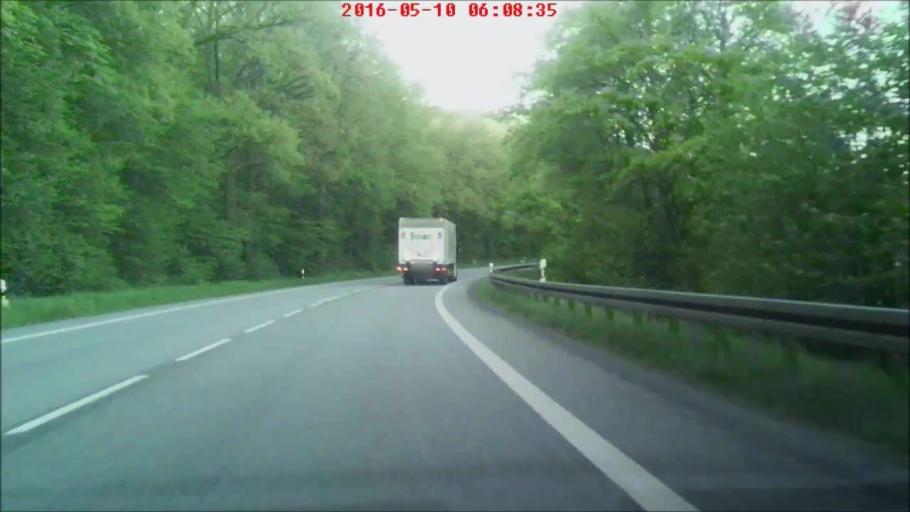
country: DE
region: Hesse
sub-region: Regierungsbezirk Kassel
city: Eiterfeld
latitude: 50.8033
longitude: 9.7360
